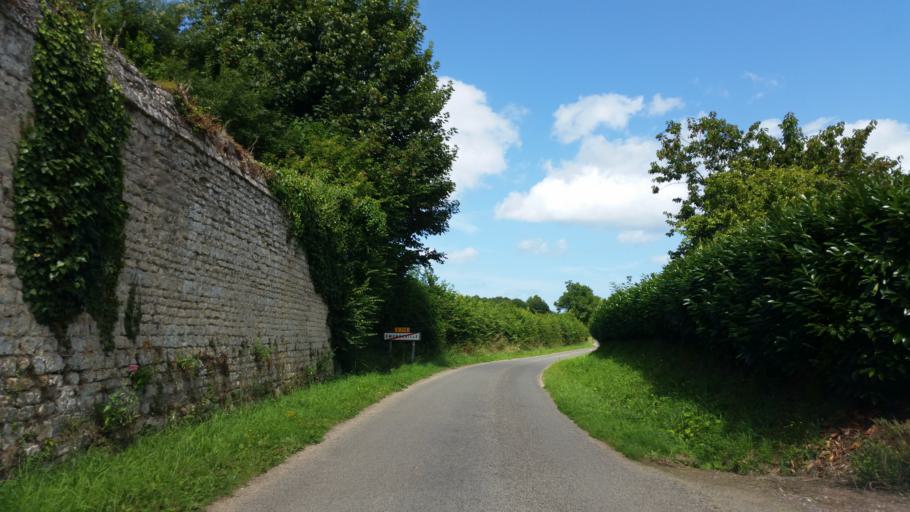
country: FR
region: Lower Normandy
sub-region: Departement de la Manche
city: Montebourg
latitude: 49.4606
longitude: -1.3409
